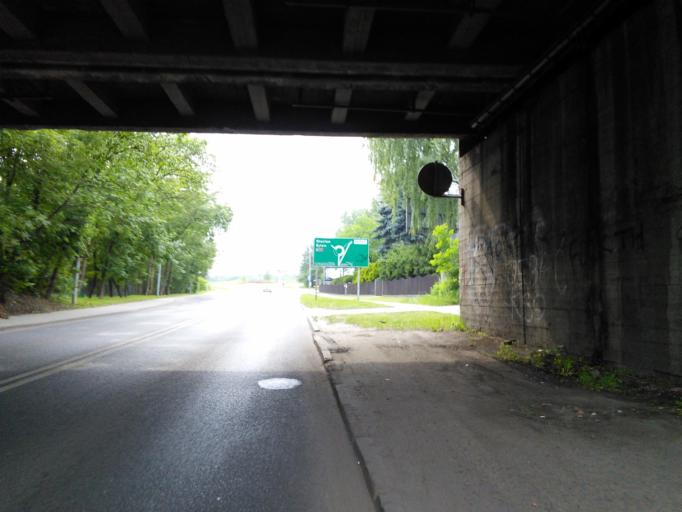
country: PL
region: Silesian Voivodeship
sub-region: Piekary Slaskie
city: Brzeziny Slaskie
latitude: 50.3713
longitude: 18.9576
